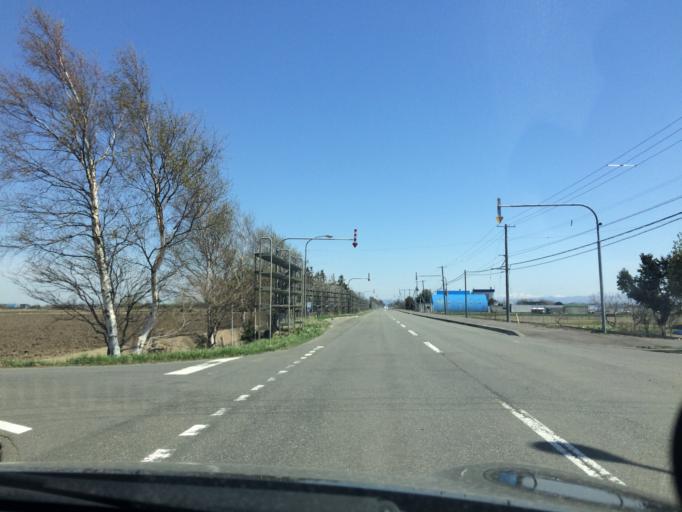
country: JP
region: Hokkaido
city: Kitahiroshima
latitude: 43.0222
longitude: 141.5846
